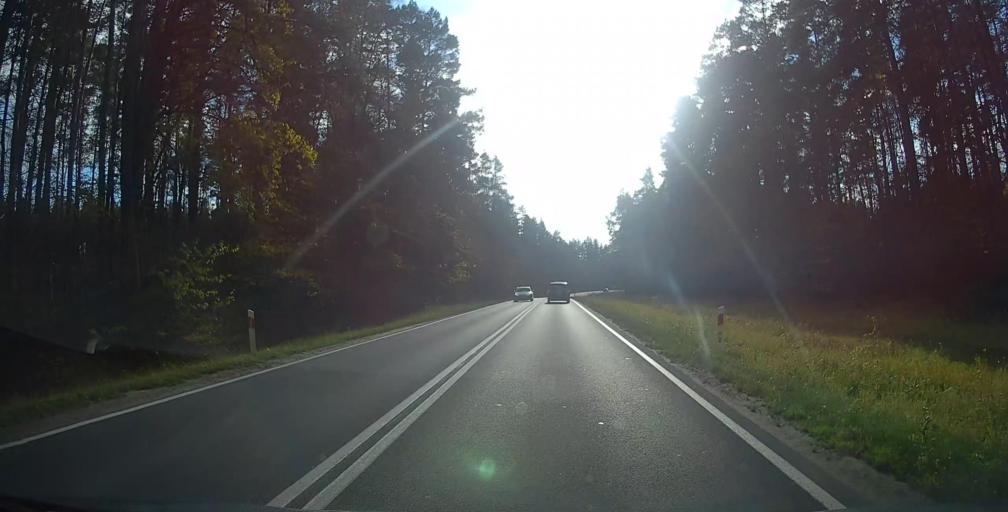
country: PL
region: Warmian-Masurian Voivodeship
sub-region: Powiat elcki
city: Elk
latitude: 53.7780
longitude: 22.3454
